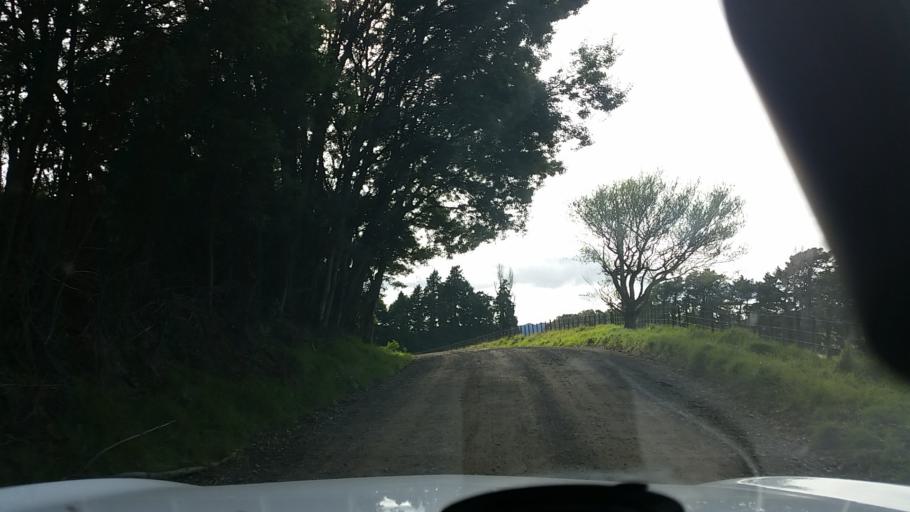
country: NZ
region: Hawke's Bay
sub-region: Napier City
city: Napier
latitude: -39.1330
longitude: 176.8956
